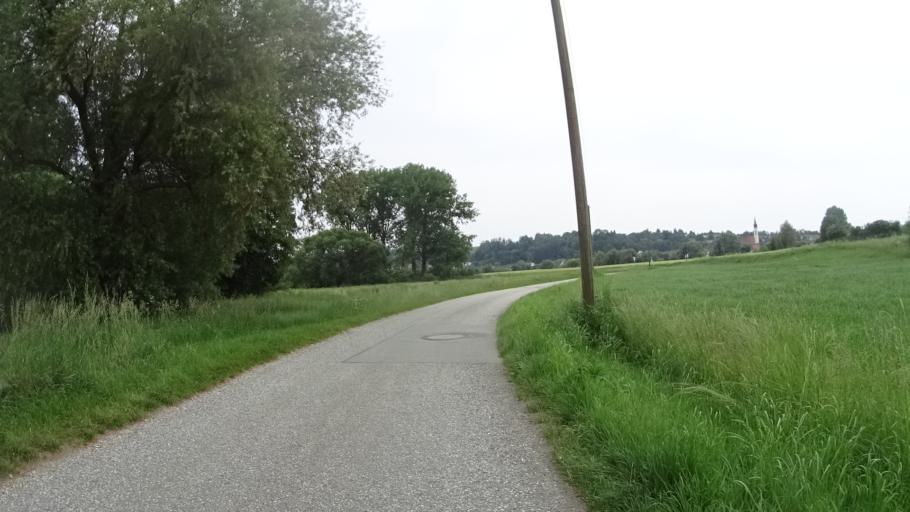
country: DE
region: Bavaria
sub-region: Lower Bavaria
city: Hofkirchen
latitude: 48.6671
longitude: 13.1244
